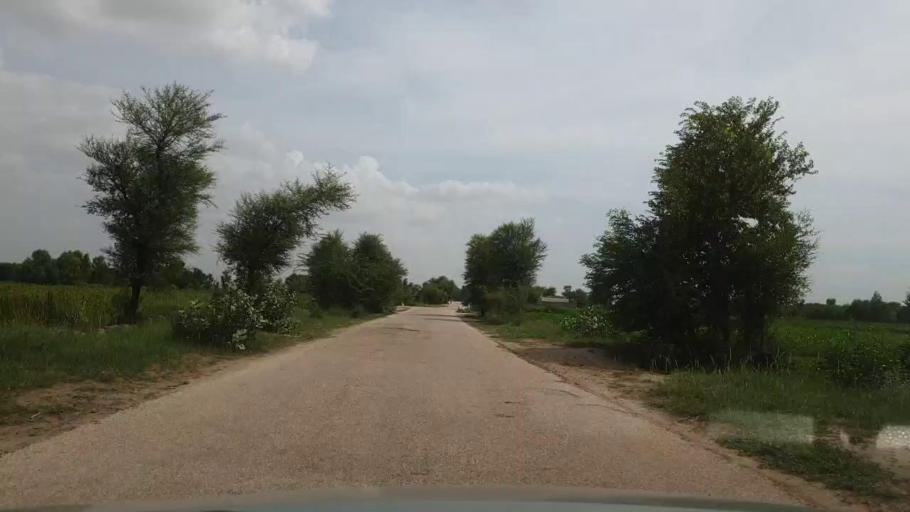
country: PK
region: Sindh
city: Kot Diji
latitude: 27.1385
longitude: 69.0281
